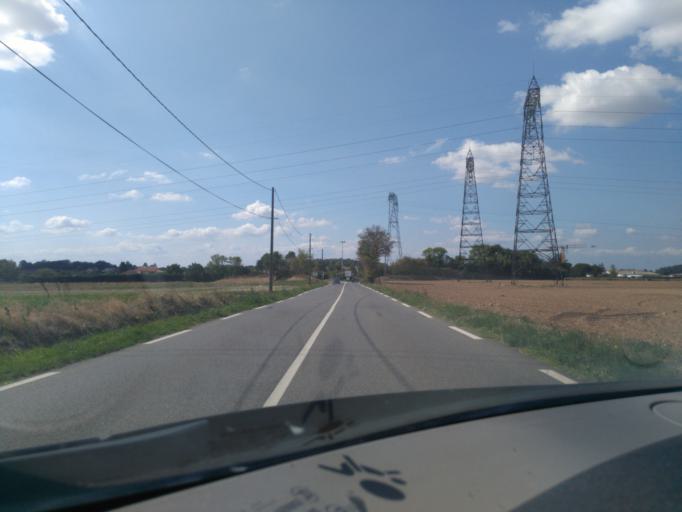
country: FR
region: Rhone-Alpes
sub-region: Departement du Rhone
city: Saint-Bonnet-de-Mure
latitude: 45.7263
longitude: 5.0319
